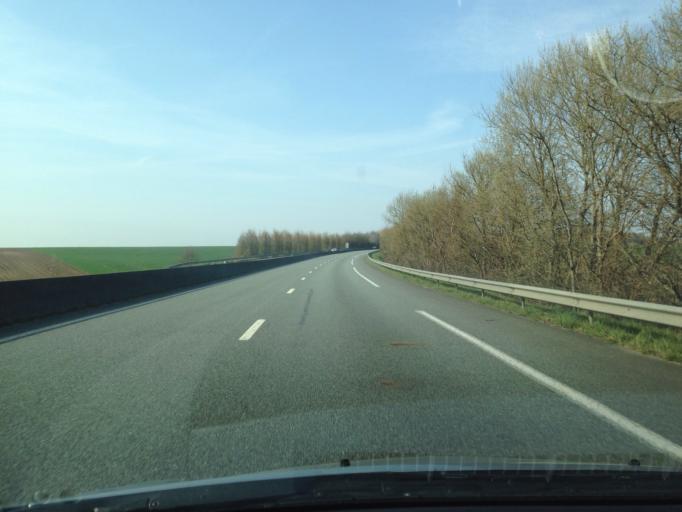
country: FR
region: Picardie
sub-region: Departement de la Somme
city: Abbeville
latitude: 50.0868
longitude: 1.7775
